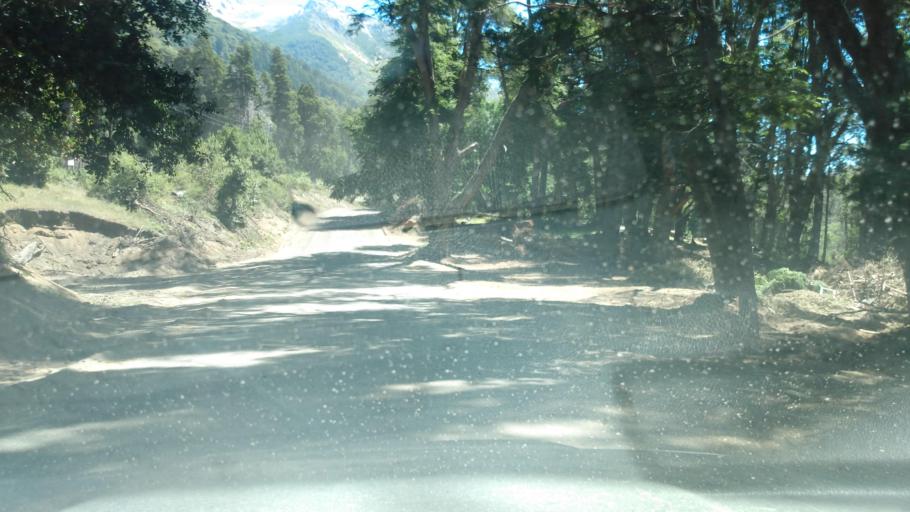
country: AR
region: Neuquen
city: Villa La Angostura
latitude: -40.6502
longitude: -71.4267
